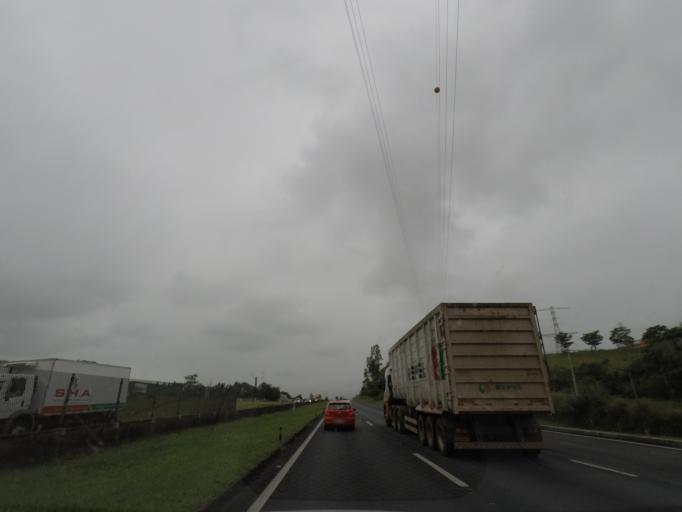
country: BR
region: Sao Paulo
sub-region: Cacapava
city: Cacapava
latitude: -23.1373
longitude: -45.7561
